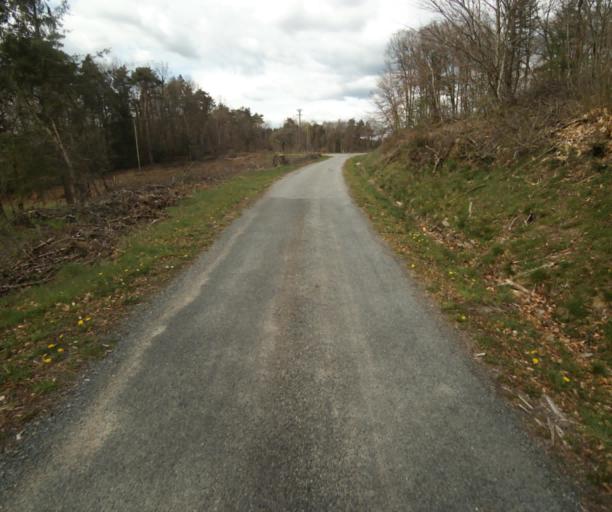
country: FR
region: Limousin
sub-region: Departement de la Correze
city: Argentat
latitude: 45.1952
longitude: 1.9468
